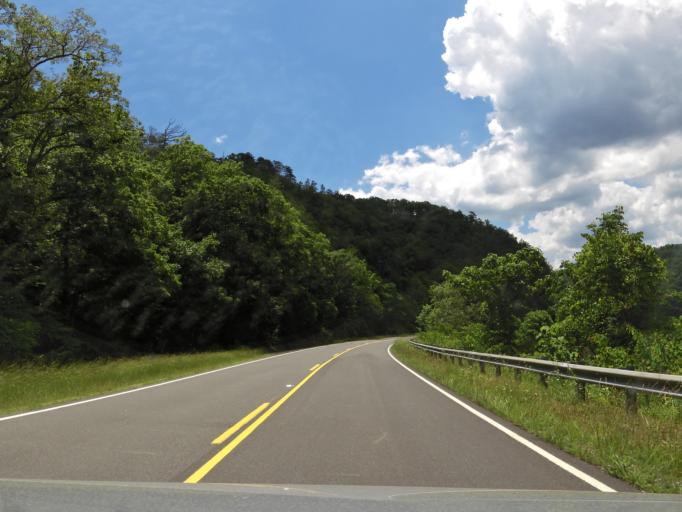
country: US
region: Tennessee
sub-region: Loudon County
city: Greenback
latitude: 35.5318
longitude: -83.9913
